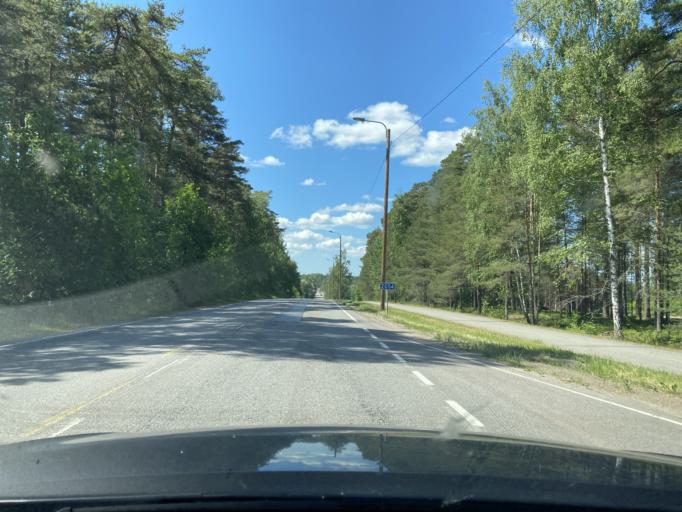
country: FI
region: Satakunta
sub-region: Rauma
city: Eura
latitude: 61.1156
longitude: 22.1596
